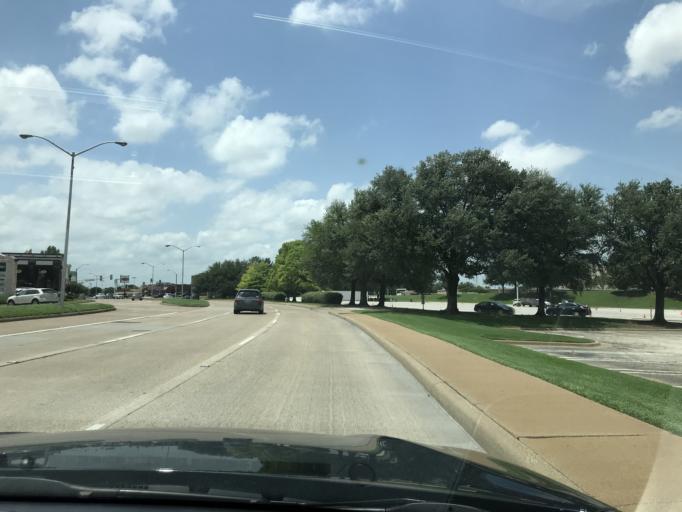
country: US
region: Texas
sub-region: Tarrant County
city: Edgecliff Village
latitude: 32.6758
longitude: -97.3985
